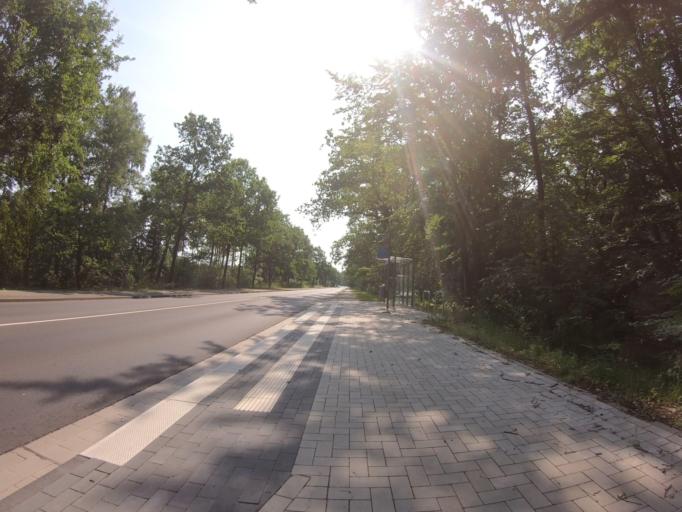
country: DE
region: Lower Saxony
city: Gifhorn
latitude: 52.4616
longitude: 10.5653
